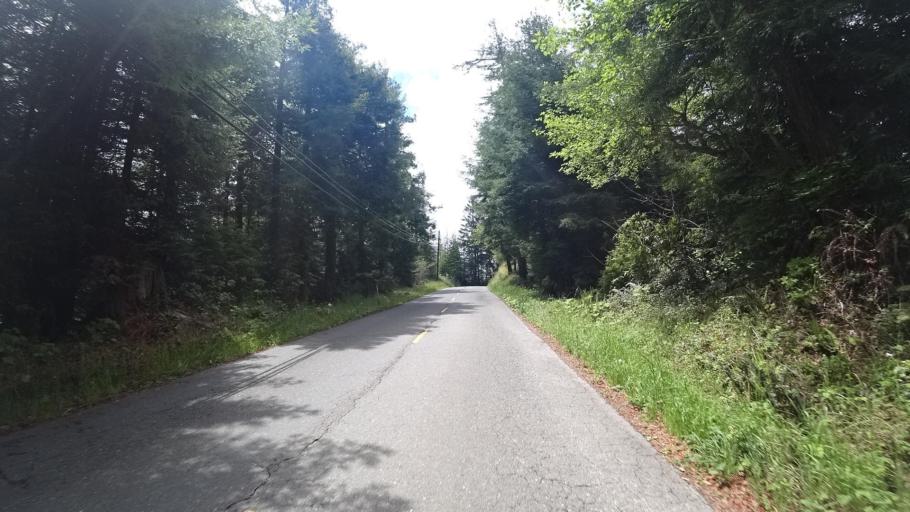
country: US
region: California
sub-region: Humboldt County
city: Bayside
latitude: 40.7874
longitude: -124.0560
